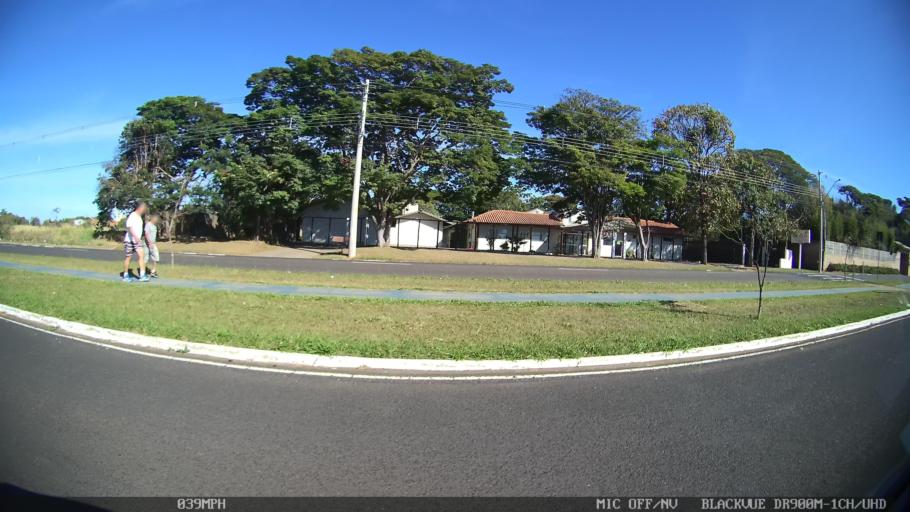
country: BR
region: Sao Paulo
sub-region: Franca
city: Franca
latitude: -20.5605
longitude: -47.3590
